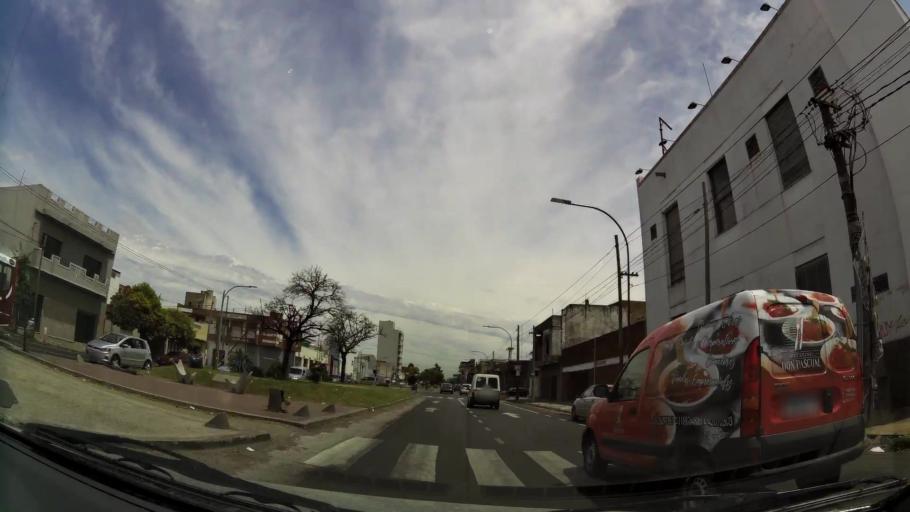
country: AR
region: Buenos Aires
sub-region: Partido de Lanus
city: Lanus
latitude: -34.6754
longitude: -58.3982
